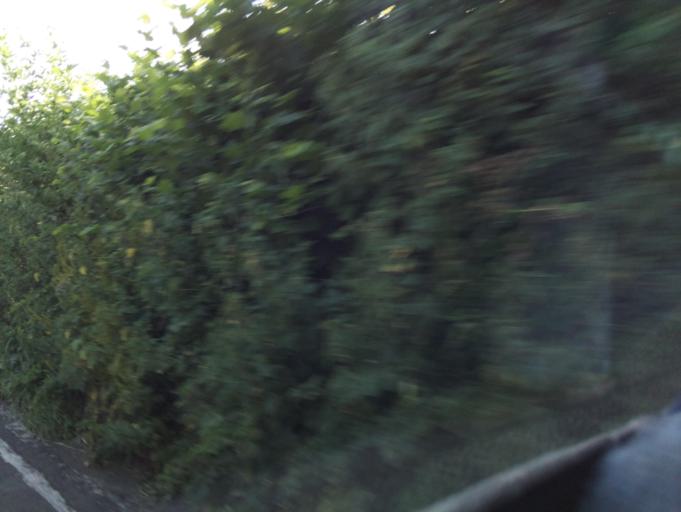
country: GB
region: England
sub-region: South Gloucestershire
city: Marshfield
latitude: 51.4871
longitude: -2.3117
